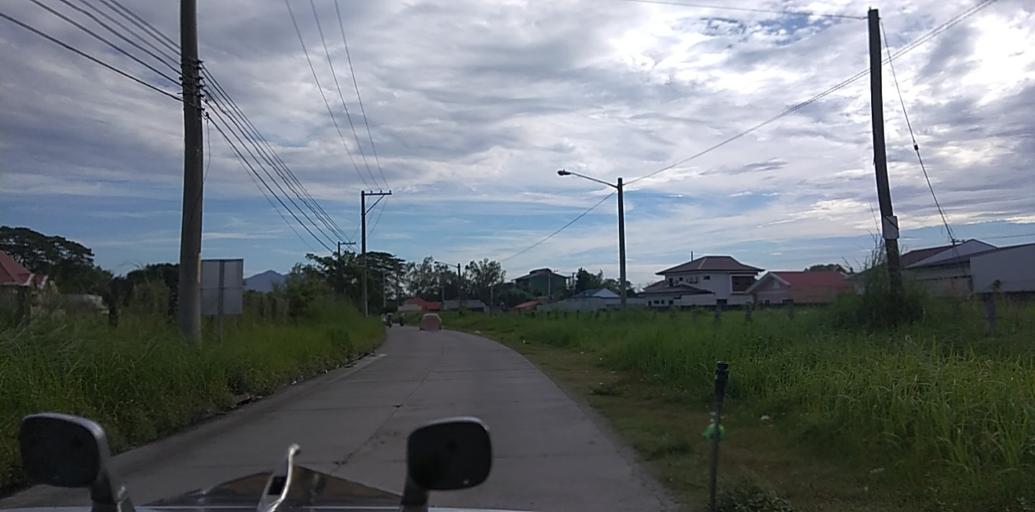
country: PH
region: Central Luzon
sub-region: Province of Pampanga
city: Telabastagan
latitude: 15.1066
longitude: 120.6094
